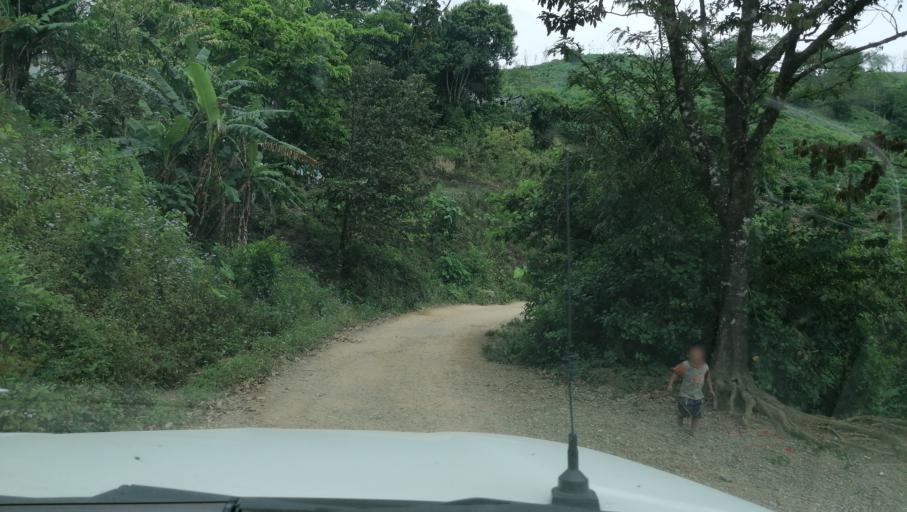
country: MX
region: Chiapas
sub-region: Francisco Leon
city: San Miguel la Sardina
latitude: 17.3445
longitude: -93.3121
